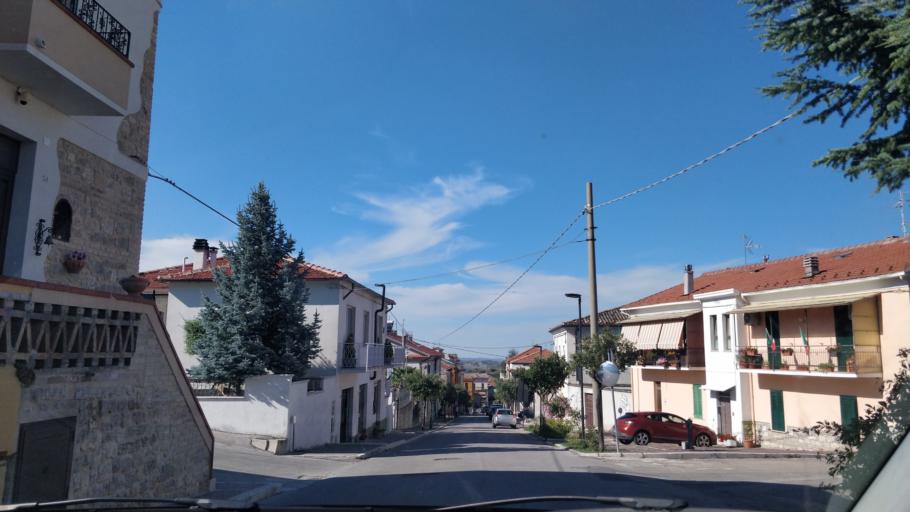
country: IT
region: Abruzzo
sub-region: Provincia di Pescara
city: Serramonacesca
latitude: 42.2470
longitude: 14.0925
